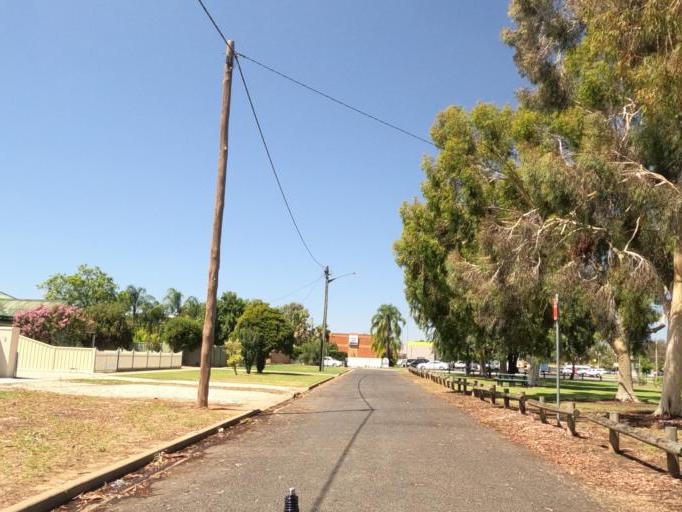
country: AU
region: New South Wales
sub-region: Corowa Shire
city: Mulwala
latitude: -35.9930
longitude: 146.0024
